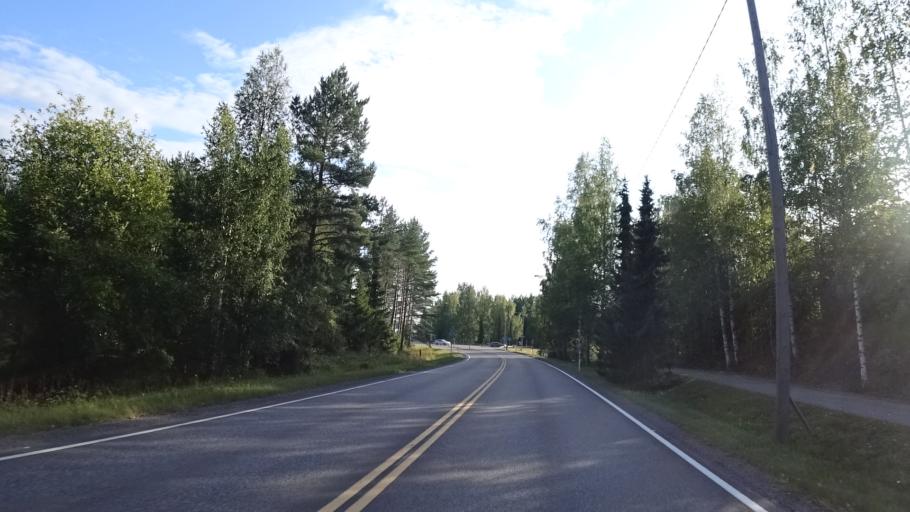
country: FI
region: South Karelia
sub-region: Imatra
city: Parikkala
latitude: 61.6045
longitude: 29.4840
